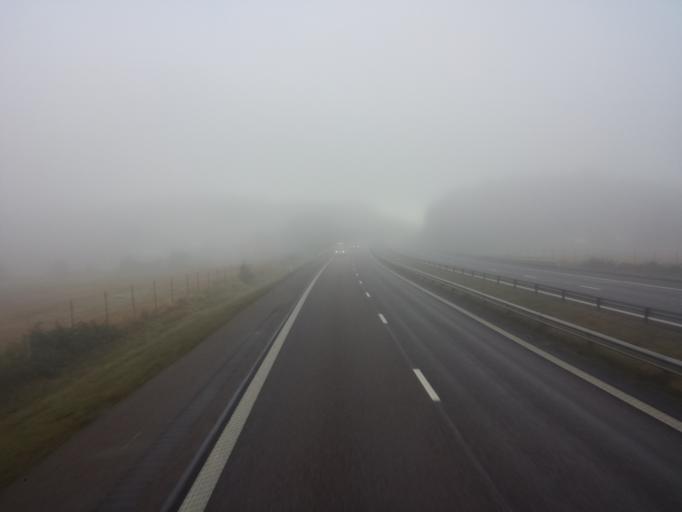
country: SE
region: Halland
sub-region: Kungsbacka Kommun
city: Fjaeras kyrkby
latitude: 57.4379
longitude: 12.1290
